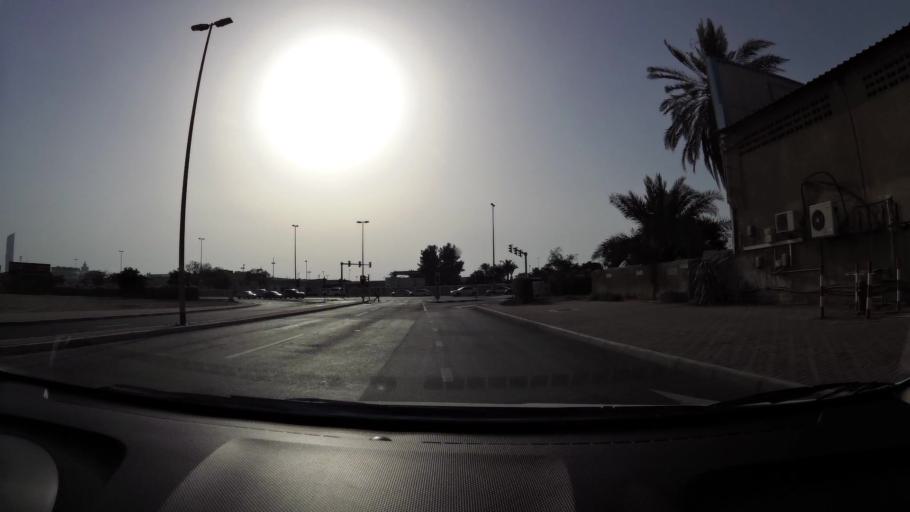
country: AE
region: Ash Shariqah
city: Sharjah
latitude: 25.2376
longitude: 55.3648
